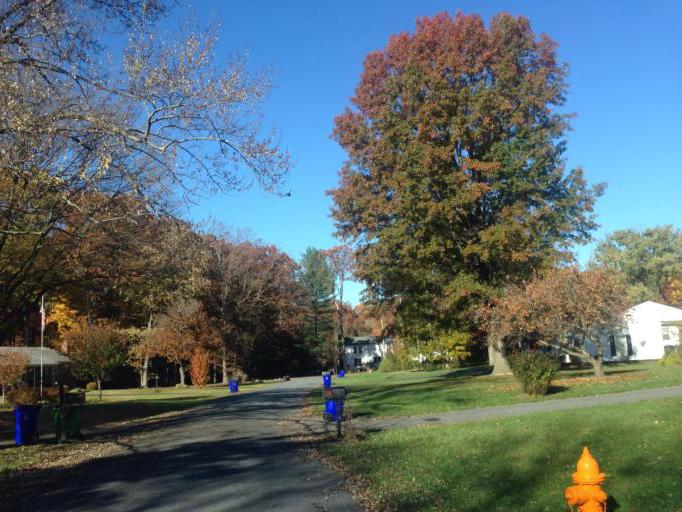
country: US
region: Maryland
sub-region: Howard County
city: Riverside
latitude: 39.1976
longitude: -76.8677
